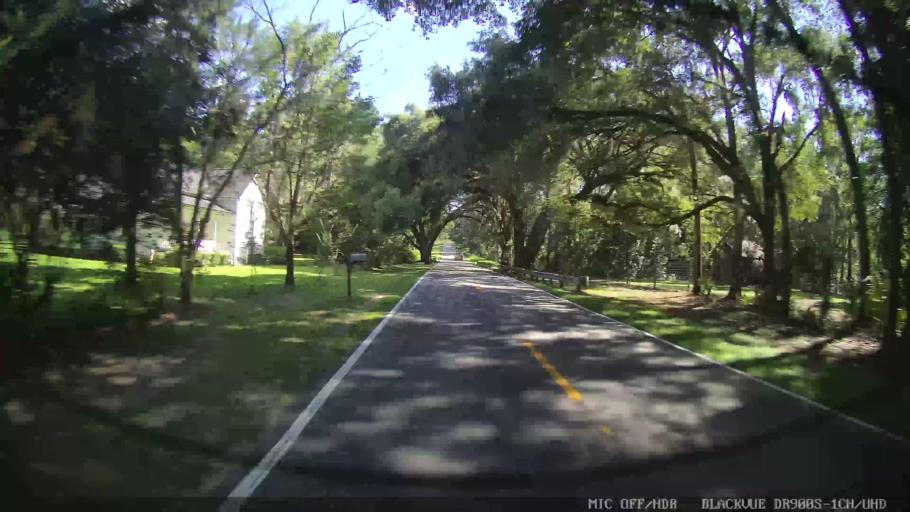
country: US
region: Georgia
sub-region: Lowndes County
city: Valdosta
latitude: 30.6415
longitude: -83.2512
